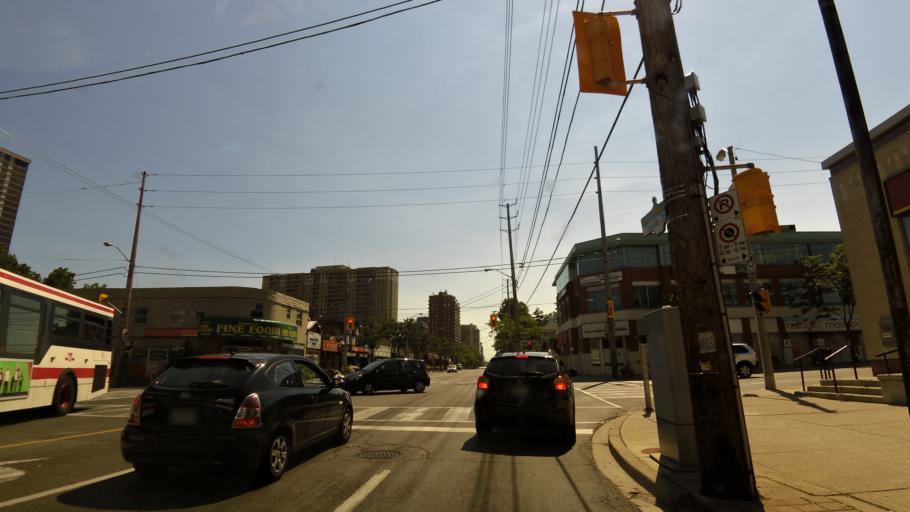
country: CA
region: Ontario
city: Etobicoke
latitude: 43.6491
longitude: -79.5286
